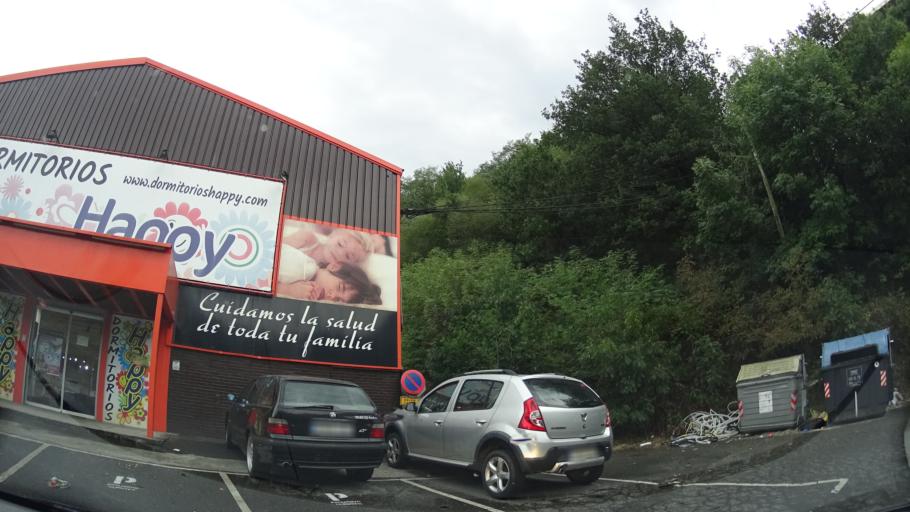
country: ES
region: Basque Country
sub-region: Bizkaia
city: Galdakao
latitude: 43.2292
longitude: -2.8188
